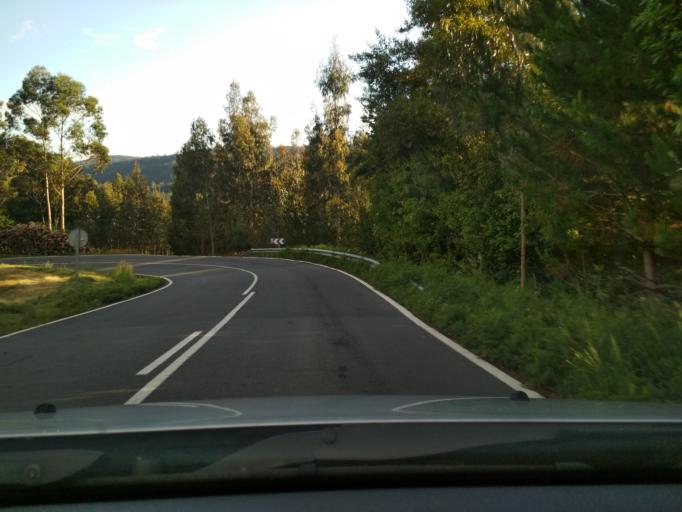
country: ES
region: Galicia
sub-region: Provincia da Coruna
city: Outes
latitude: 42.8920
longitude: -8.9313
